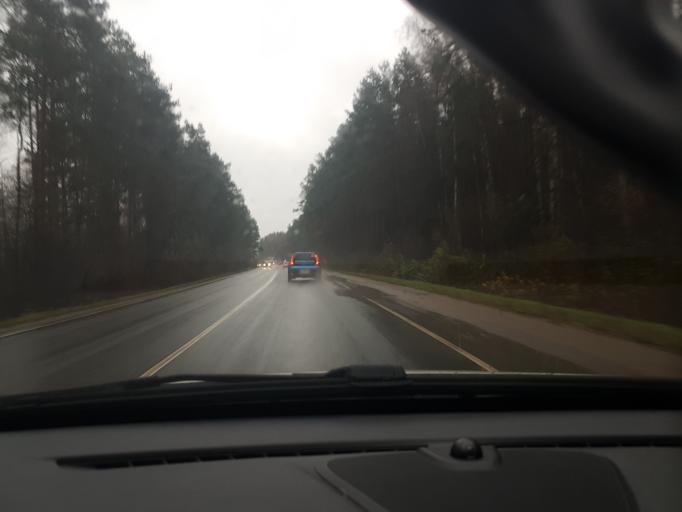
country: RU
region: Moskovskaya
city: Snegiri
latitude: 55.8526
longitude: 36.9421
